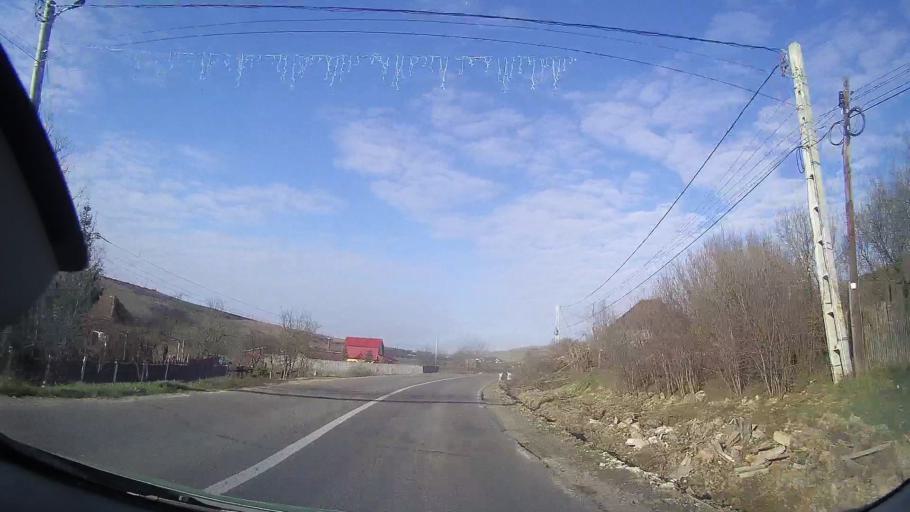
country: RO
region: Cluj
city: Caianu Mic
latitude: 46.7999
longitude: 23.8746
